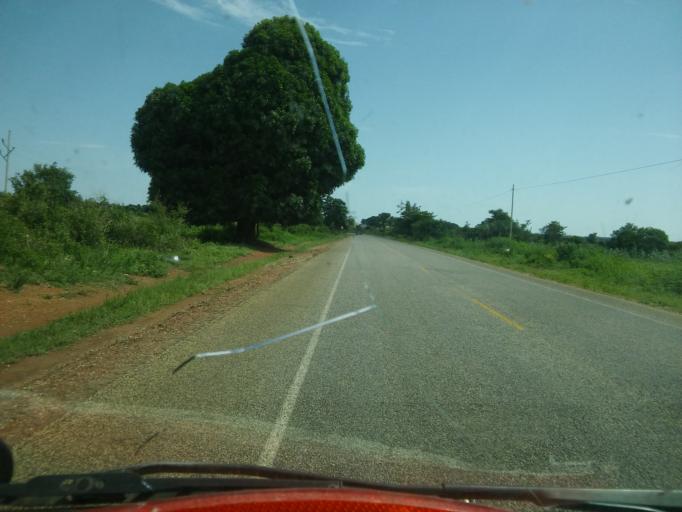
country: UG
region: Eastern Region
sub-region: Bukedea District
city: Bukedea
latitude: 1.3344
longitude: 34.0551
